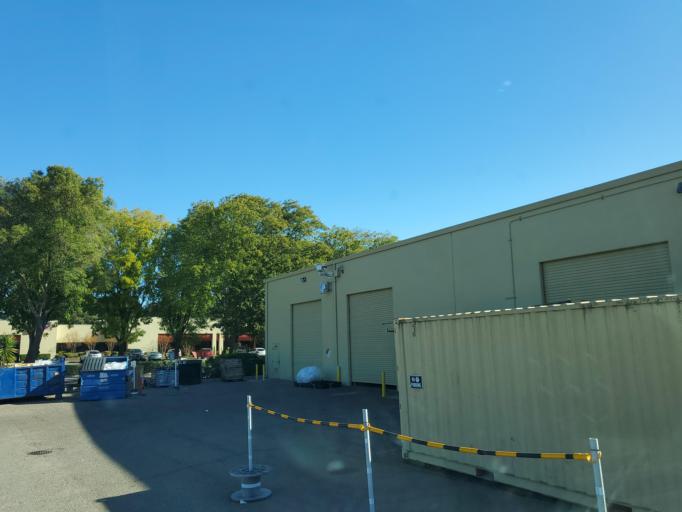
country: US
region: California
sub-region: San Joaquin County
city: French Camp
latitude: 37.8975
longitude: -121.2791
